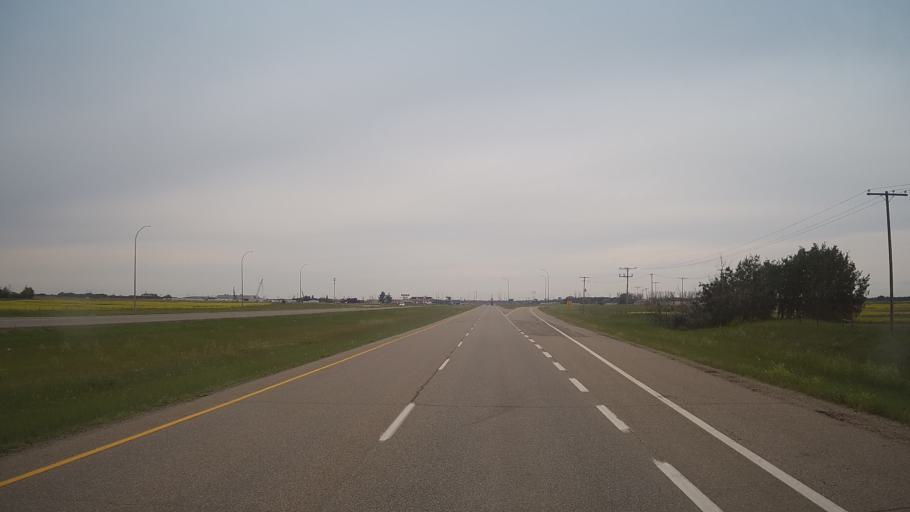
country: CA
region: Saskatchewan
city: Saskatoon
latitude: 52.0472
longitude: -106.5933
